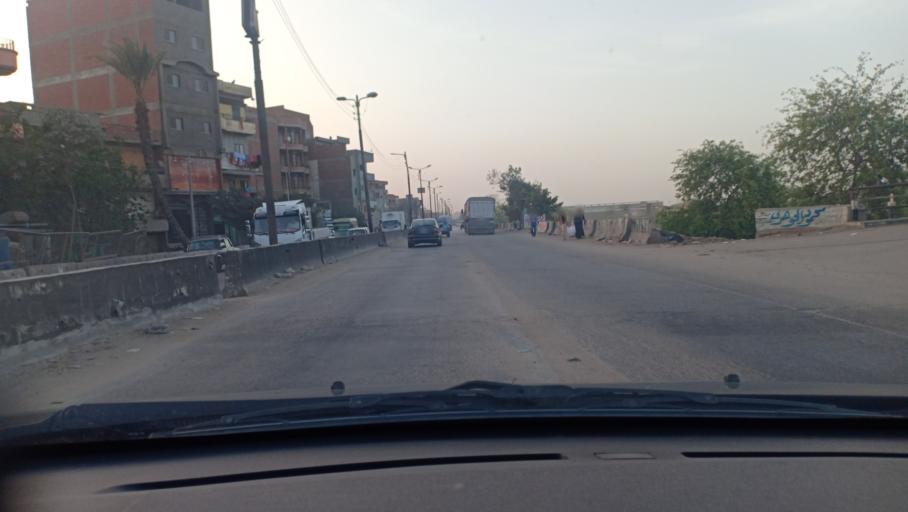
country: EG
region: Muhafazat al Gharbiyah
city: Zifta
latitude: 30.6825
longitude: 31.2815
